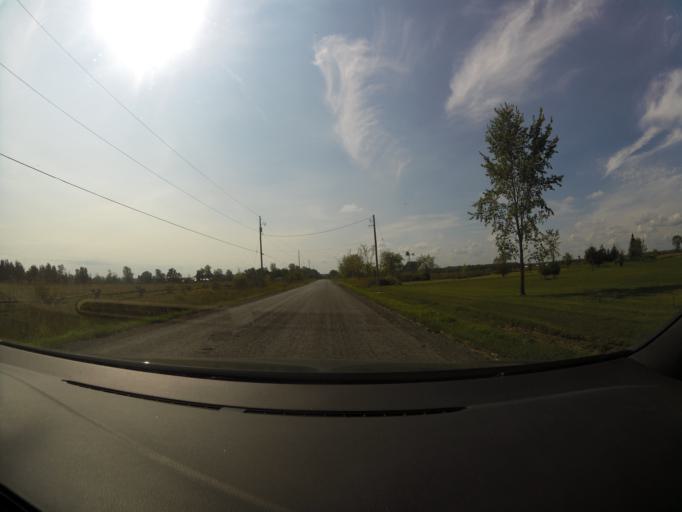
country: CA
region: Ontario
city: Carleton Place
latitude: 45.2897
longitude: -76.2325
